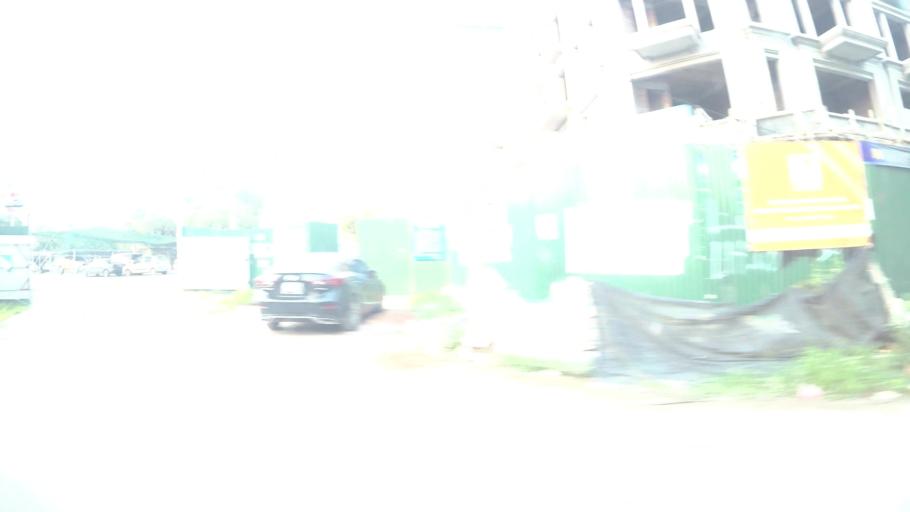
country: VN
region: Ha Noi
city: Thanh Xuan
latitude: 20.9757
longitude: 105.8213
